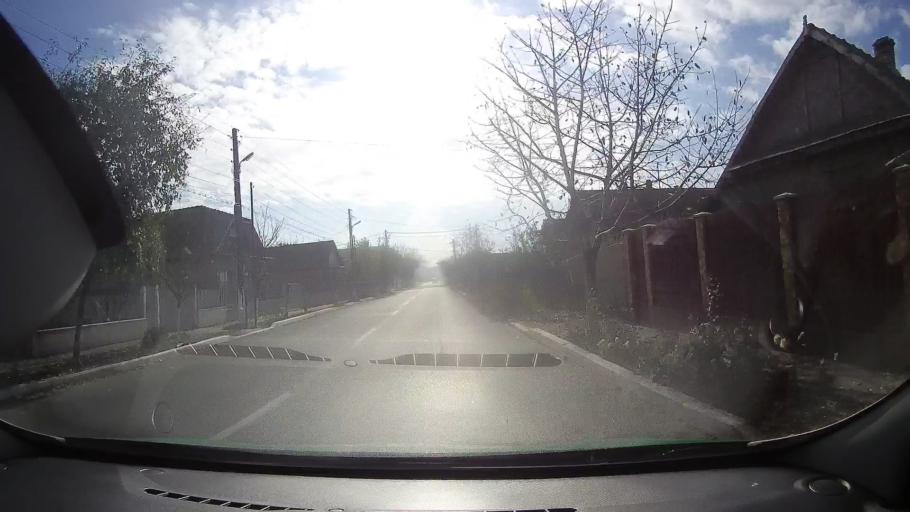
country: RO
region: Tulcea
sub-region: Comuna Sarichioi
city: Sarichioi
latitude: 44.9466
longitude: 28.8528
